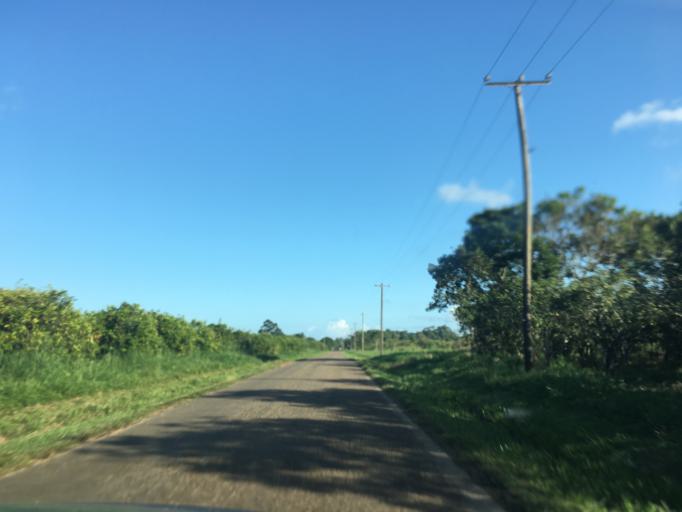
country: BZ
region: Stann Creek
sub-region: Dangriga
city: Dangriga
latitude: 16.8213
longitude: -88.3378
